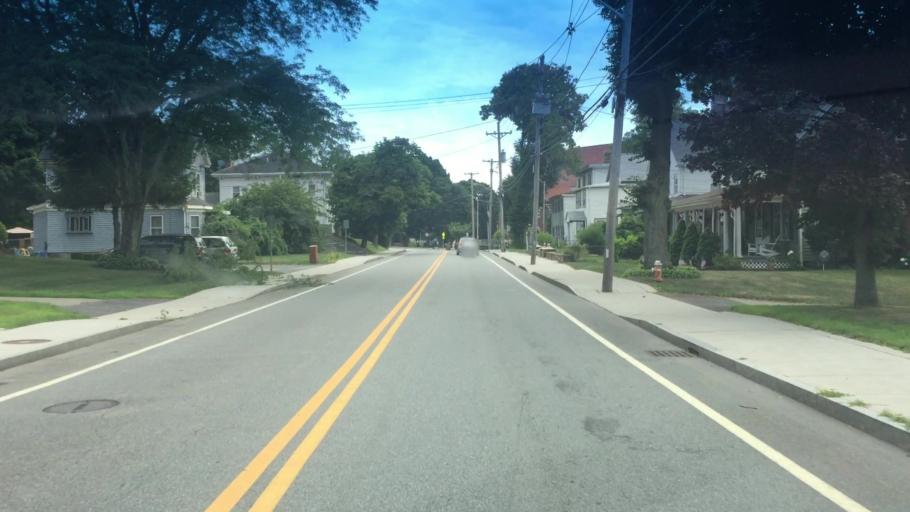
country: US
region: Massachusetts
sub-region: Norfolk County
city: Franklin
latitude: 42.0911
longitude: -71.4004
